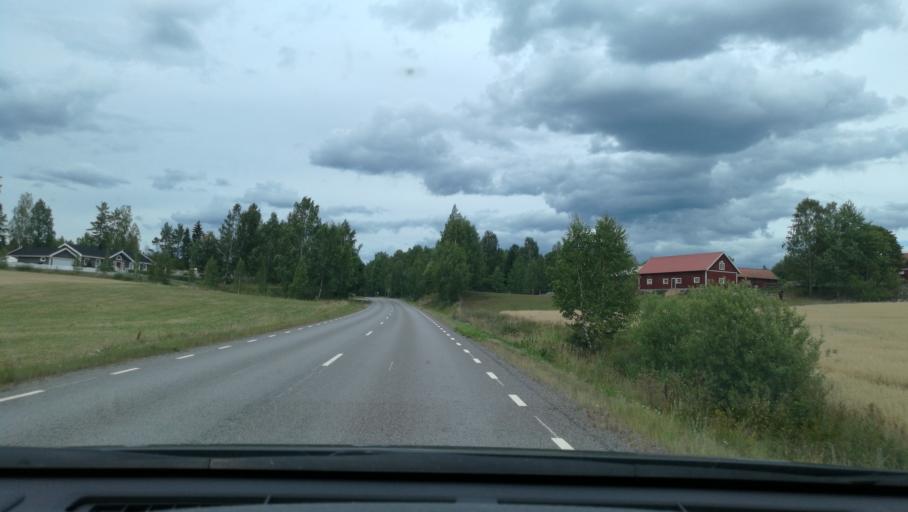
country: SE
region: OEstergoetland
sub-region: Norrkopings Kommun
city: Svartinge
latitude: 58.7158
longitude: 15.9395
